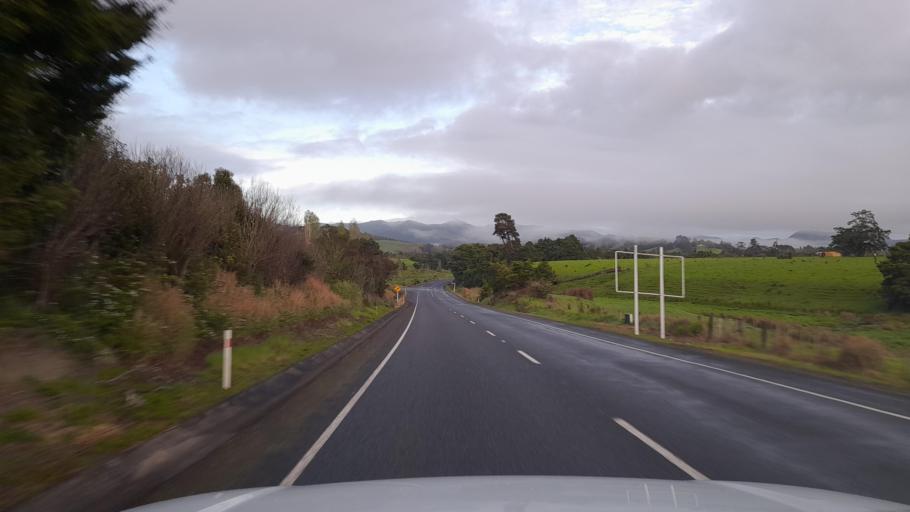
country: NZ
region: Northland
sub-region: Kaipara District
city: Dargaville
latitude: -35.7146
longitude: 173.9508
